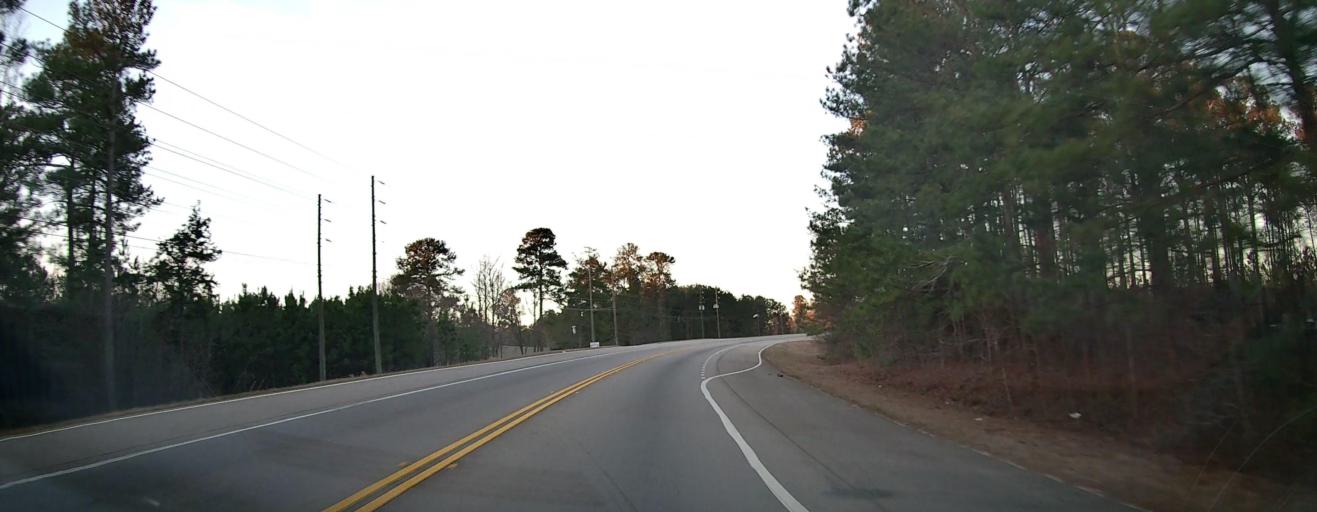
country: US
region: Georgia
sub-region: Troup County
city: La Grange
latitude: 33.0343
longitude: -84.9879
